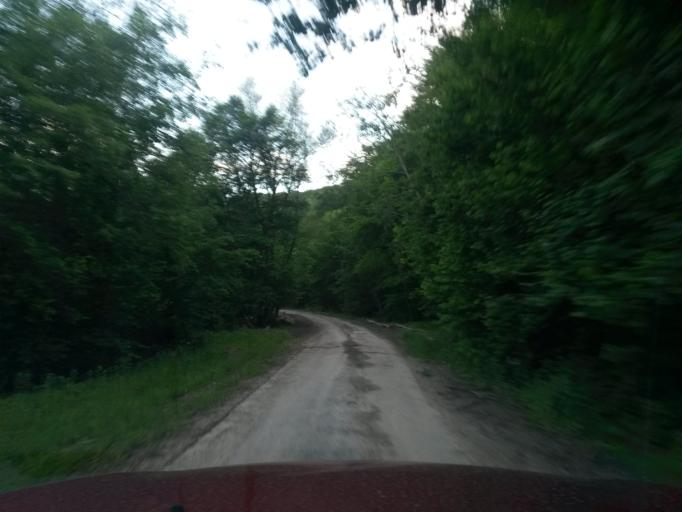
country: UA
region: Zakarpattia
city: Velykyi Bereznyi
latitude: 48.8471
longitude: 22.3591
